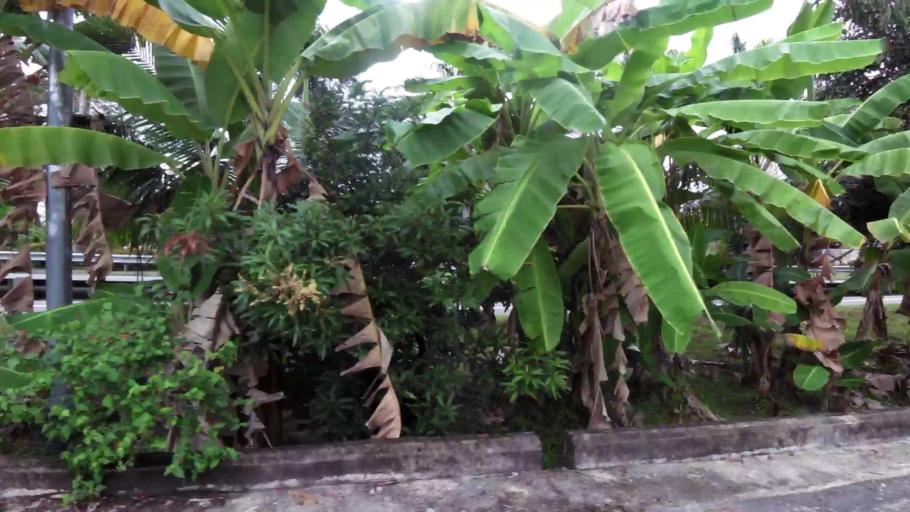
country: BN
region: Brunei and Muara
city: Bandar Seri Begawan
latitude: 4.8947
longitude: 114.9275
